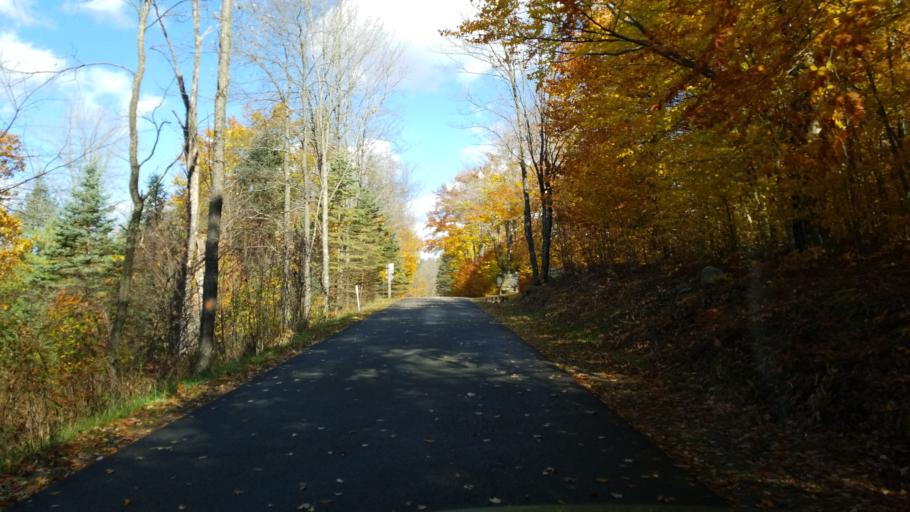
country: US
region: Pennsylvania
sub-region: Clearfield County
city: Clearfield
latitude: 41.1958
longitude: -78.5064
